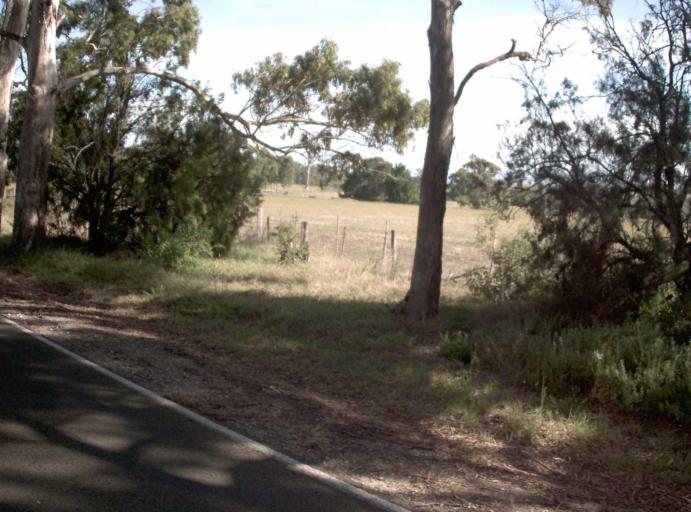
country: AU
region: Victoria
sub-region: East Gippsland
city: Lakes Entrance
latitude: -37.8099
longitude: 147.8444
